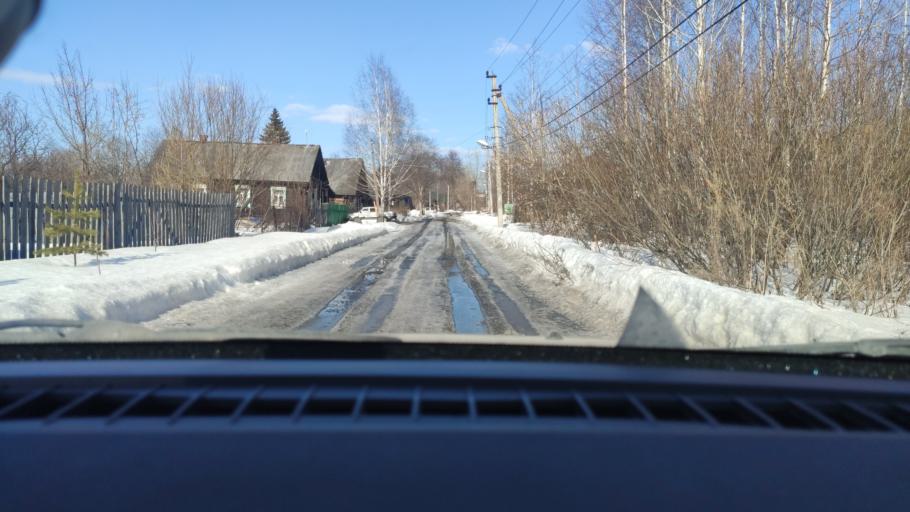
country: RU
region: Perm
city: Perm
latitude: 58.0642
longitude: 56.3394
